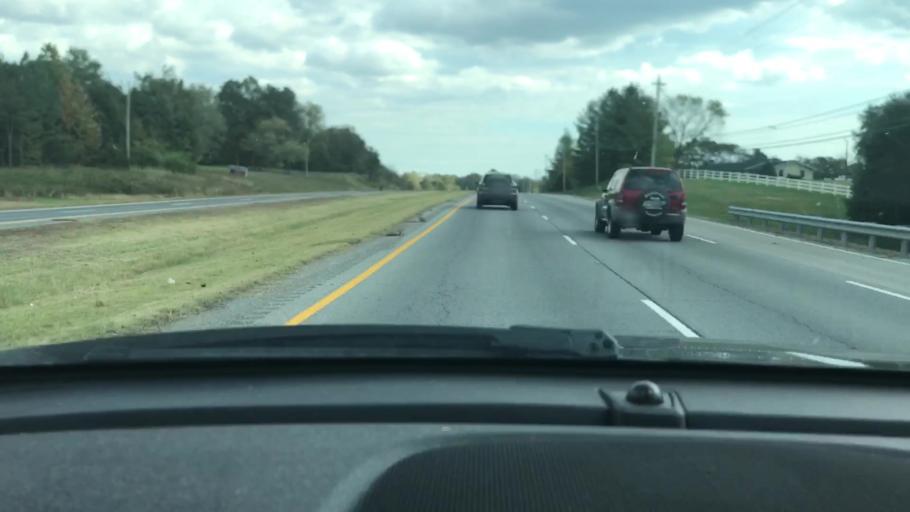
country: US
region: Tennessee
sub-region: Cheatham County
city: Ashland City
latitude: 36.2259
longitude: -87.0093
